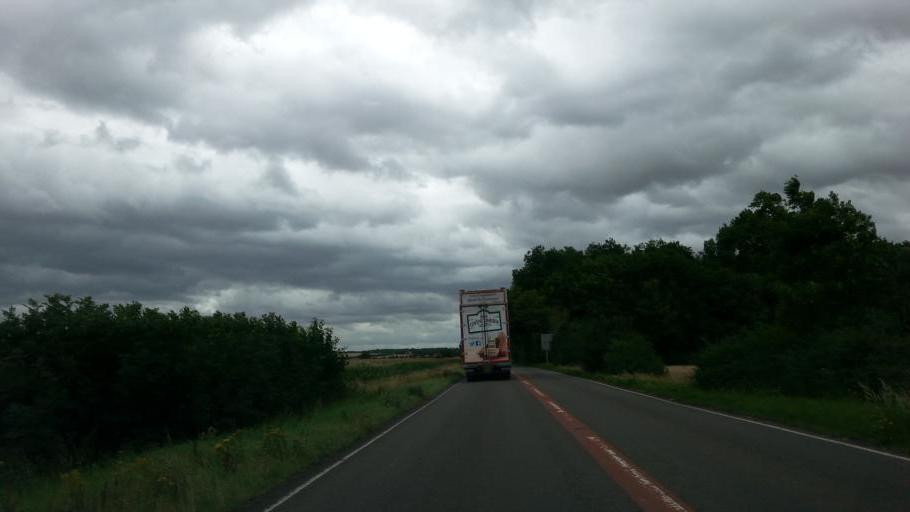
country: GB
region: England
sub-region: Cambridgeshire
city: Papworth Everard
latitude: 52.2750
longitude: -0.1369
